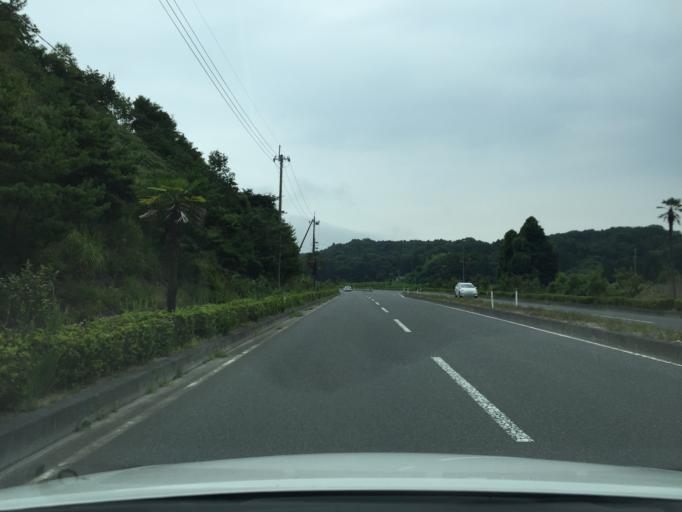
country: JP
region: Fukushima
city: Iwaki
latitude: 36.9584
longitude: 140.9191
